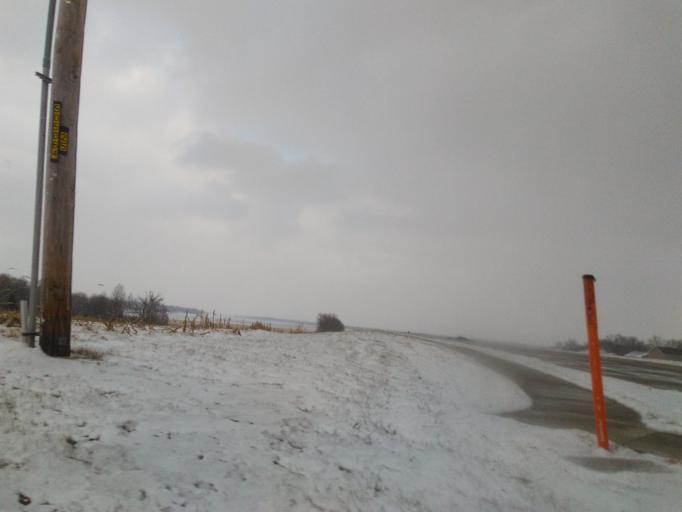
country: US
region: Illinois
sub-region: Bond County
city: Greenville
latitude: 38.8932
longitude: -89.3911
